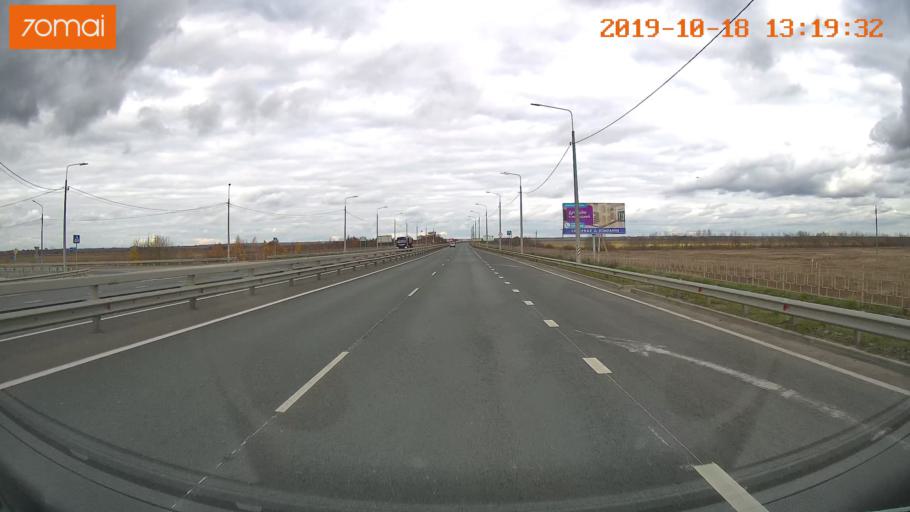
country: RU
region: Rjazan
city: Polyany
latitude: 54.6685
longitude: 39.8256
